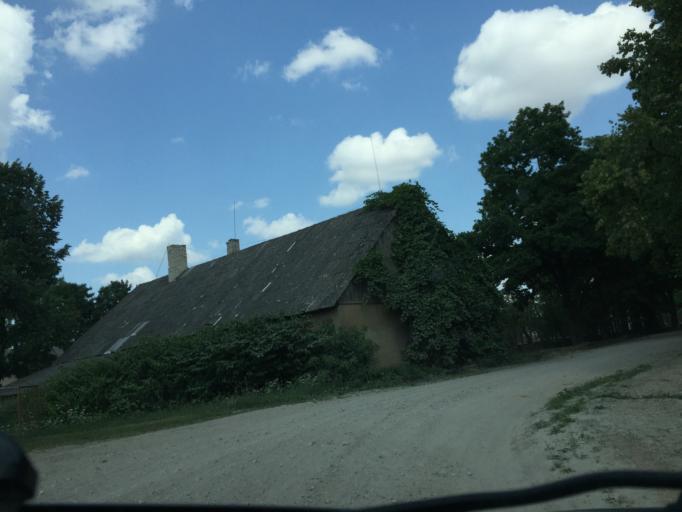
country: LT
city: Zagare
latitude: 56.3991
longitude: 23.2492
